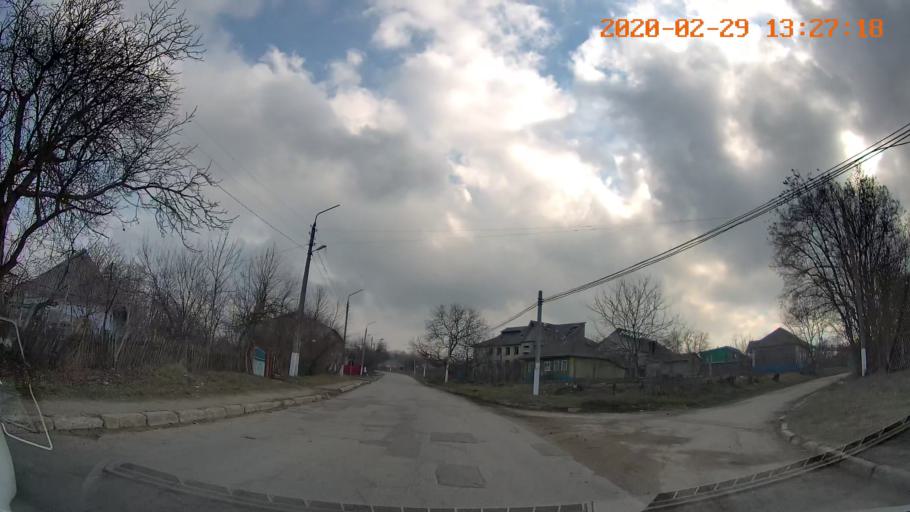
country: MD
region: Telenesti
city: Camenca
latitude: 47.9128
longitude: 28.6400
